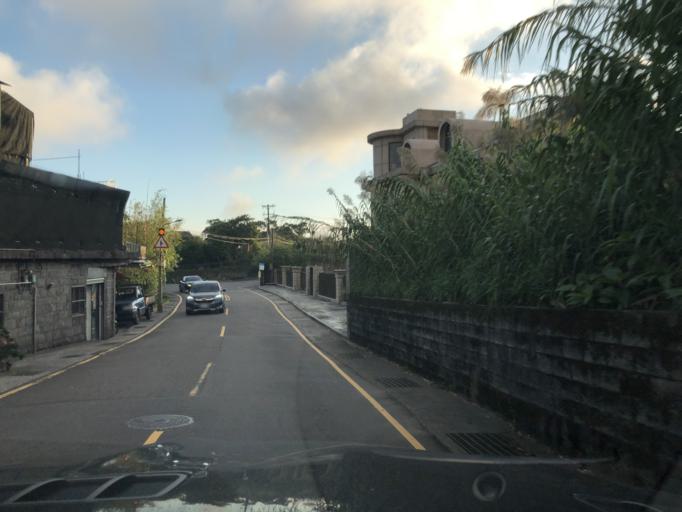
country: TW
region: Taipei
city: Taipei
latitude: 25.1477
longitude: 121.5586
